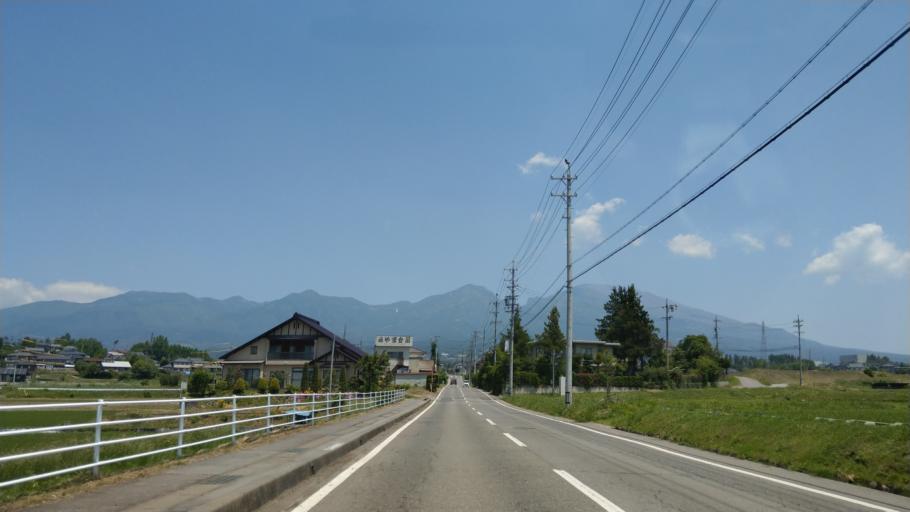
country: JP
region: Nagano
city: Komoro
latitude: 36.3037
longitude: 138.4390
